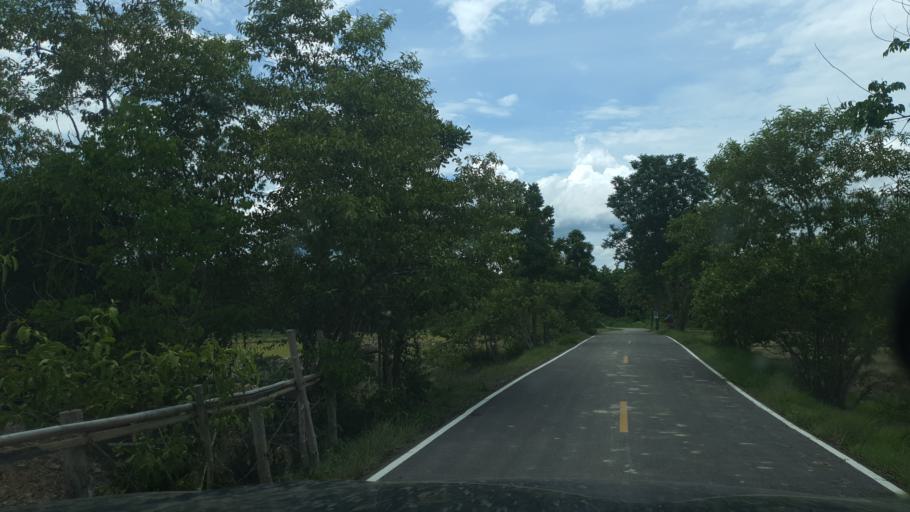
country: TH
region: Lampang
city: Sop Prap
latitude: 17.8672
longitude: 99.3895
